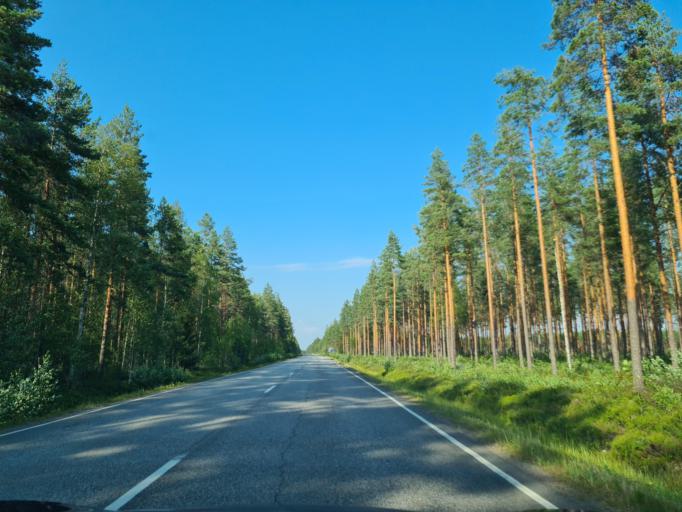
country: FI
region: Satakunta
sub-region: Pohjois-Satakunta
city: Karvia
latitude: 62.2995
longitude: 22.6317
